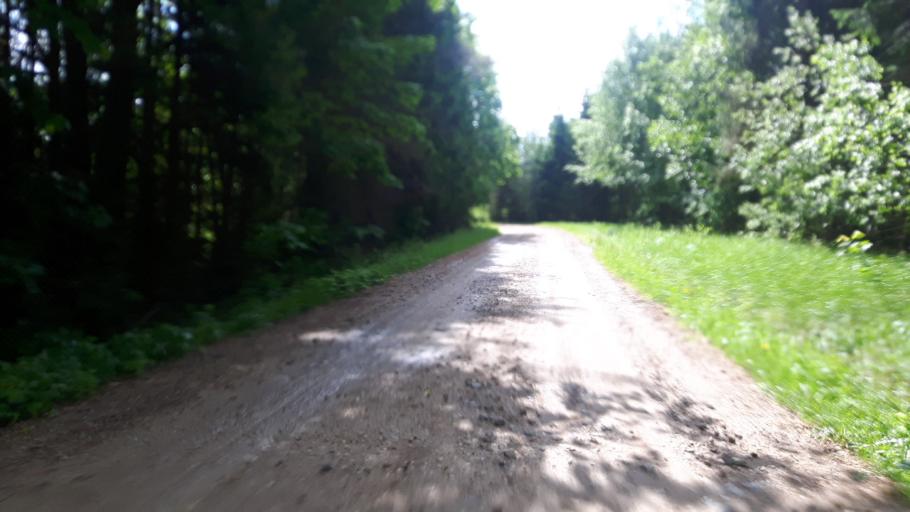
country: EE
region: Paernumaa
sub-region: Vaendra vald (alev)
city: Vandra
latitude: 58.7293
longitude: 25.0123
